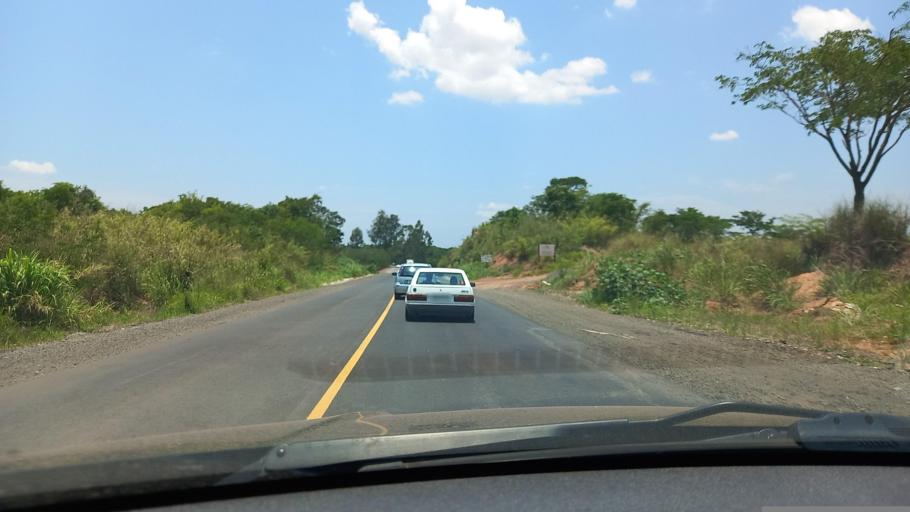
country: BR
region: Sao Paulo
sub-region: Moji-Guacu
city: Mogi-Gaucu
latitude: -22.3741
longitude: -46.8751
